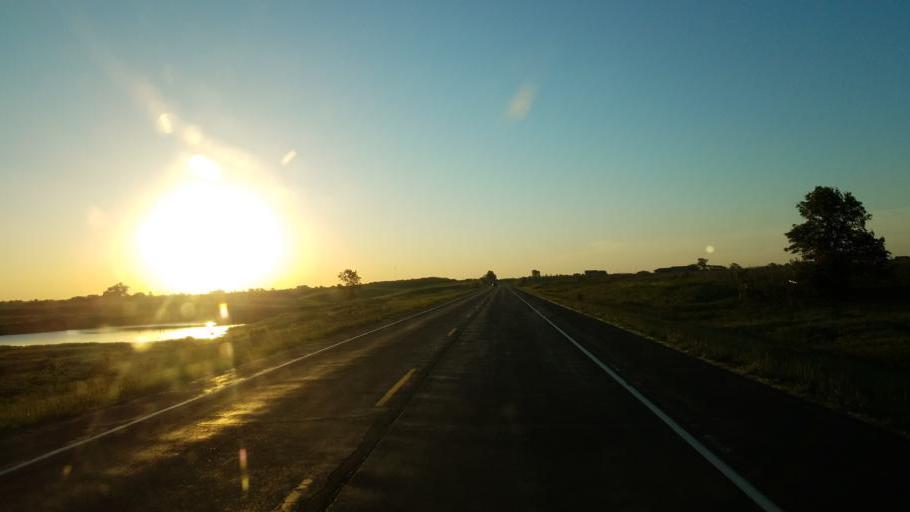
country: US
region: Missouri
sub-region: Schuyler County
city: Lancaster
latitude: 40.4928
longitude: -92.5685
